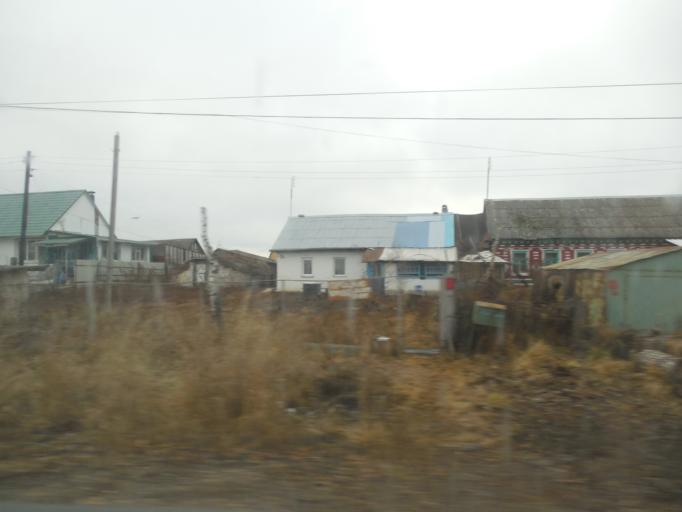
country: RU
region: Tula
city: Dubovka
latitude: 53.9009
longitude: 38.0357
